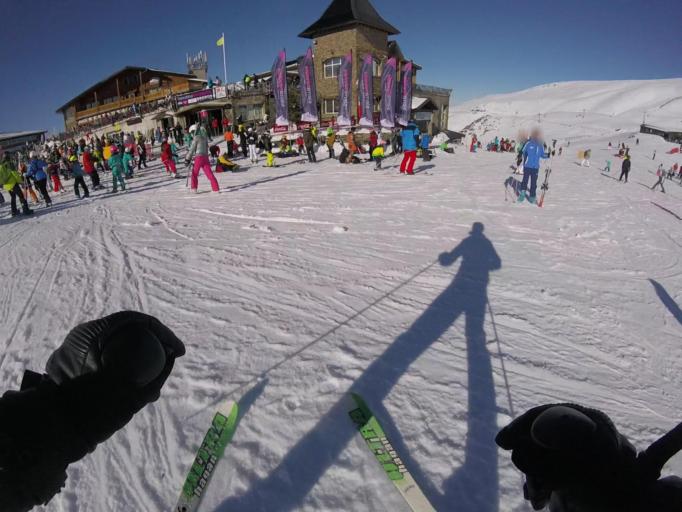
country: ES
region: Andalusia
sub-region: Provincia de Granada
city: Guejar-Sierra
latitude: 37.0711
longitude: -3.3879
